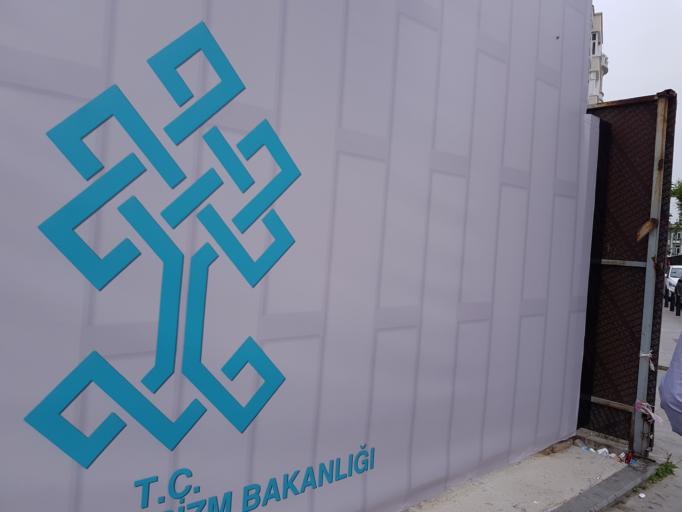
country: TR
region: Istanbul
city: Eminoenue
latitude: 41.0365
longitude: 28.9874
